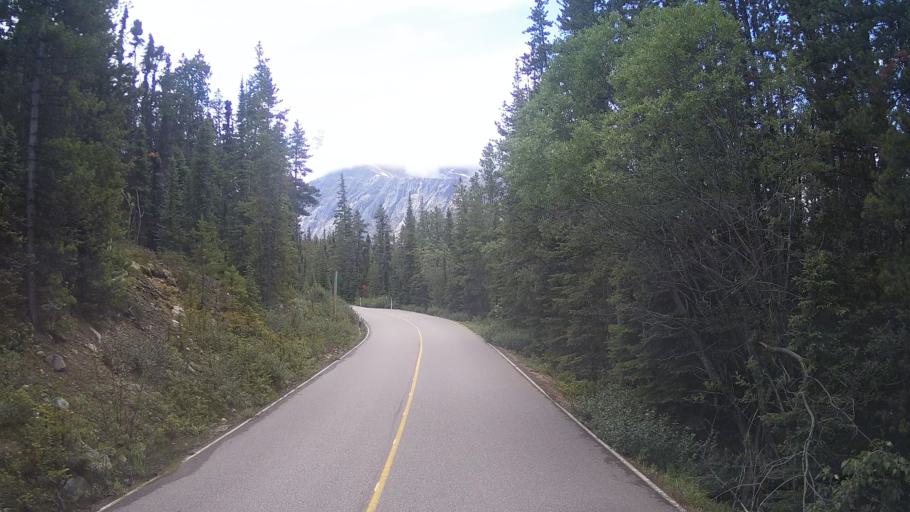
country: CA
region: Alberta
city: Jasper Park Lodge
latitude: 52.7229
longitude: -118.0513
